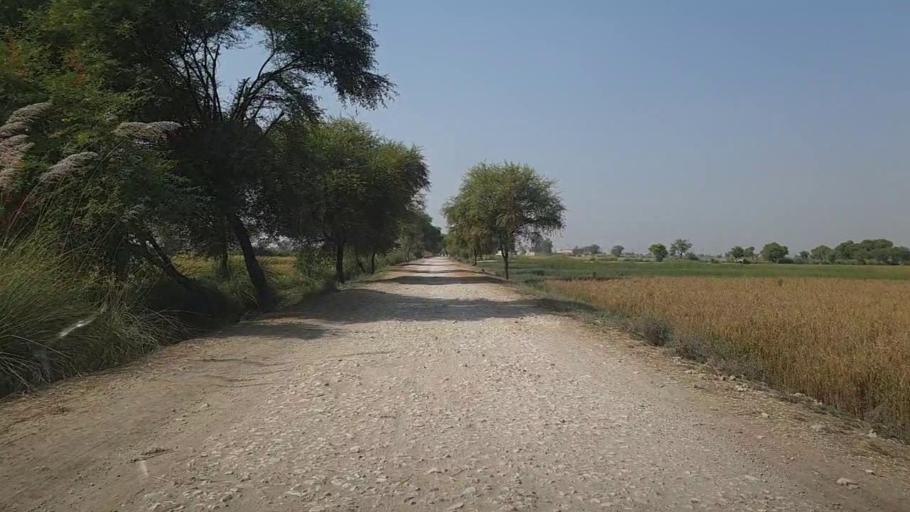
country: PK
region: Sindh
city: Kandhkot
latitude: 28.3942
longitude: 69.2985
